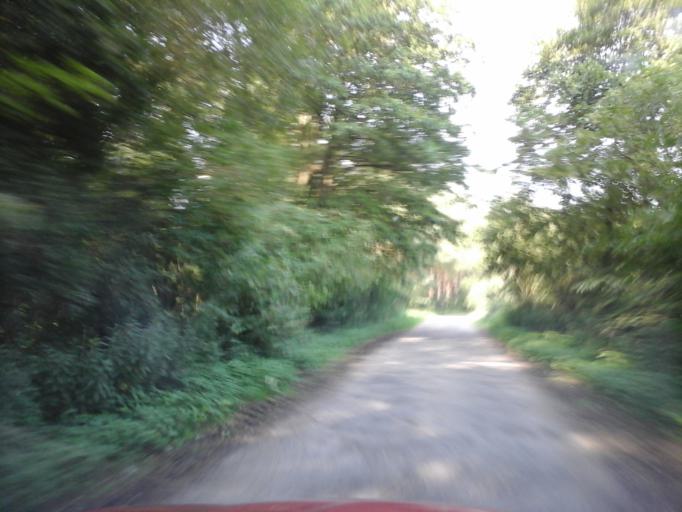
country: PL
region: West Pomeranian Voivodeship
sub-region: Powiat mysliborski
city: Barlinek
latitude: 53.0677
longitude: 15.2250
